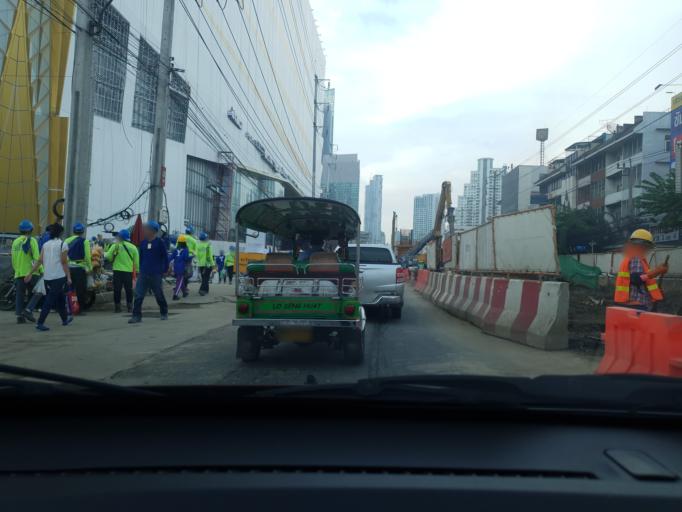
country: TH
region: Bangkok
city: Khlong San
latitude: 13.7278
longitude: 100.5090
